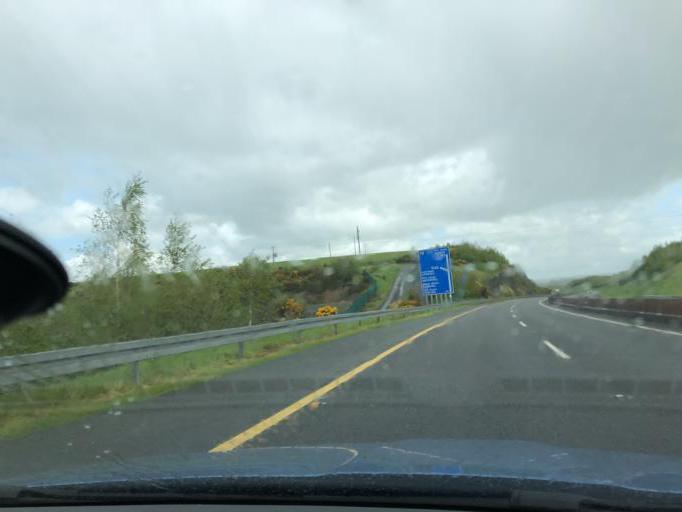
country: IE
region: Munster
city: Cahir
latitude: 52.3897
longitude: -7.9347
